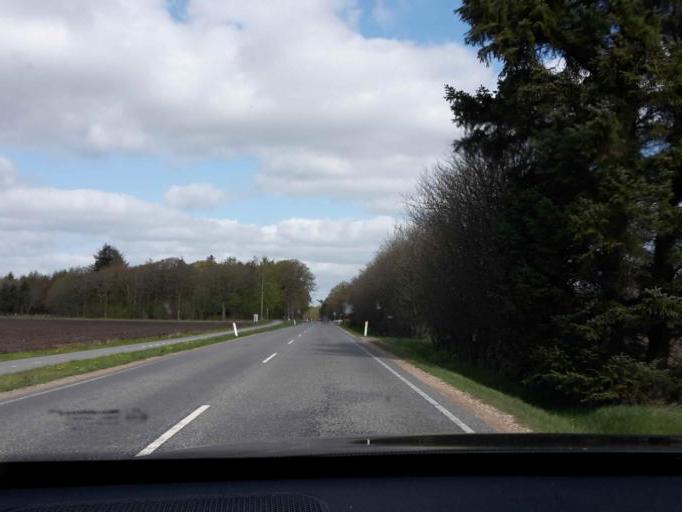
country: DK
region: South Denmark
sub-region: Varde Kommune
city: Olgod
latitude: 55.7187
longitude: 8.7351
